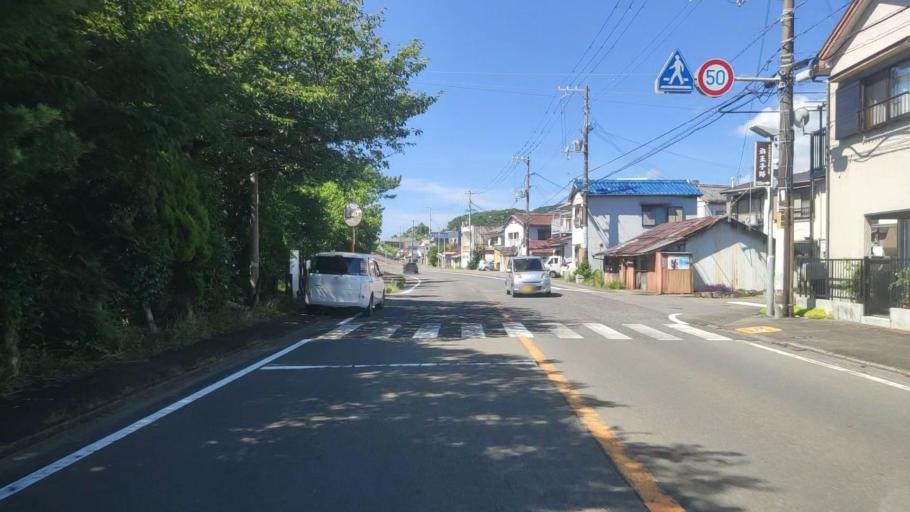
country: JP
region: Wakayama
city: Shingu
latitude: 33.7165
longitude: 136.0028
